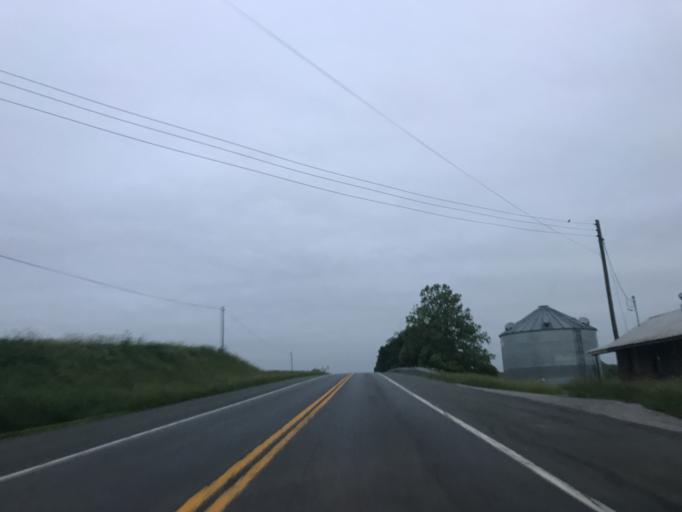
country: US
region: Maryland
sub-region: Frederick County
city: Linganore
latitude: 39.4613
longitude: -77.2476
